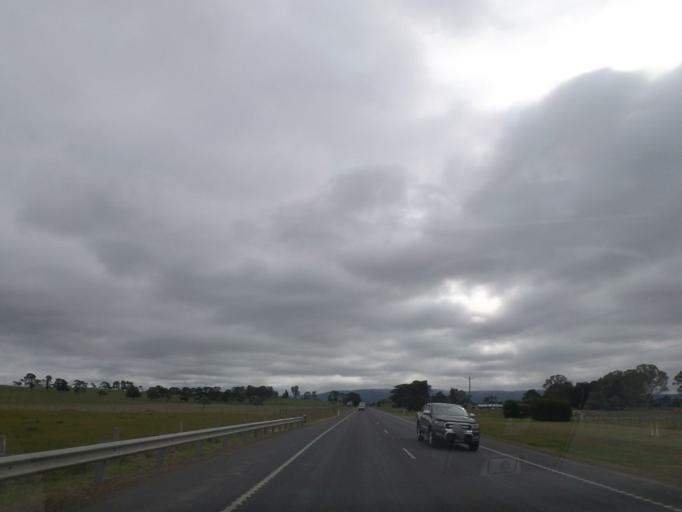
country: AU
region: Victoria
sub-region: Whittlesea
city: Whittlesea
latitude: -37.5470
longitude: 145.1092
